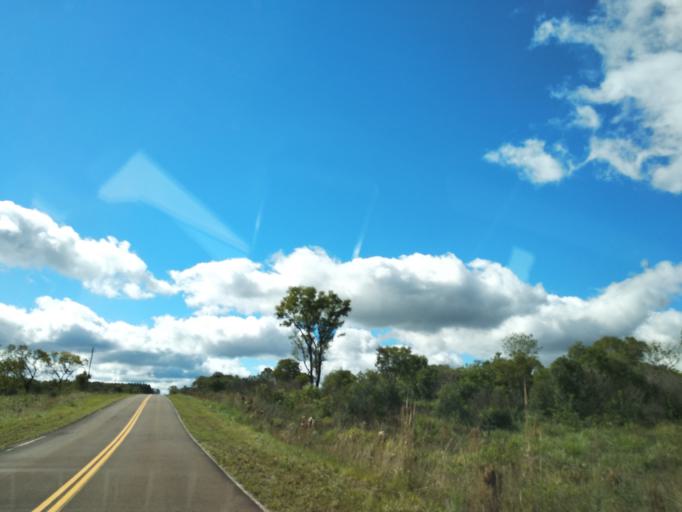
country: AR
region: Misiones
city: Santa Ana
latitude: -27.4121
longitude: -55.5595
